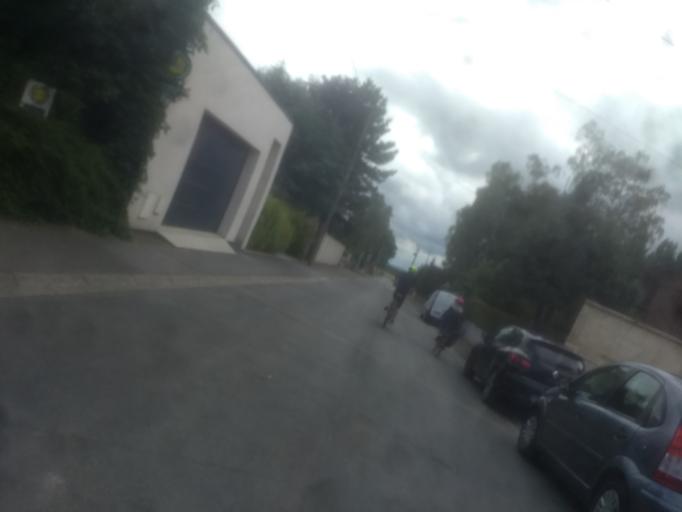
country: FR
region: Nord-Pas-de-Calais
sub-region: Departement du Pas-de-Calais
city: Thelus
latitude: 50.3525
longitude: 2.8000
